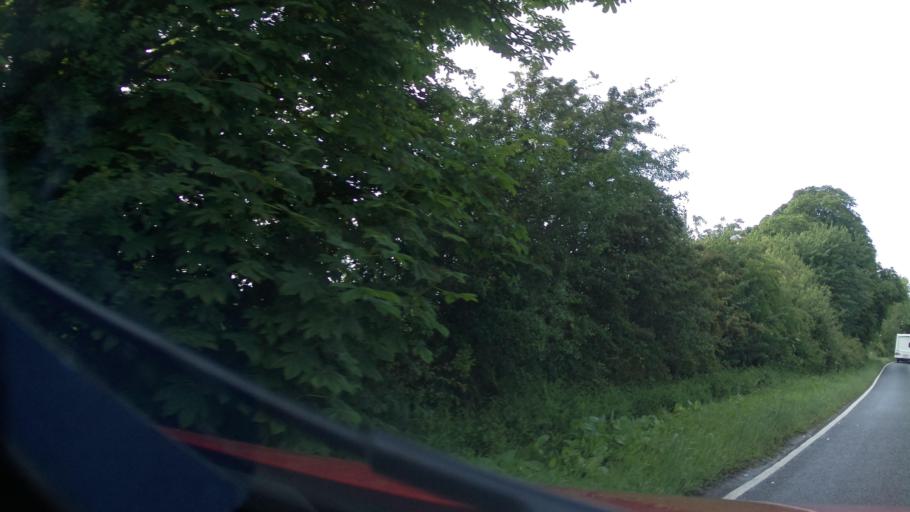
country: GB
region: England
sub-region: Lincolnshire
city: Great Gonerby
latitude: 53.0187
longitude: -0.6581
